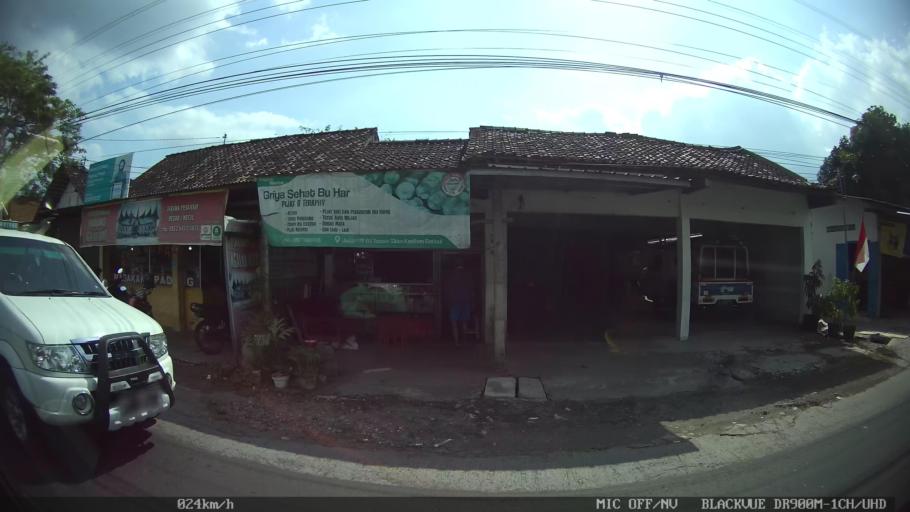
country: ID
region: Daerah Istimewa Yogyakarta
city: Kasihan
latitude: -7.8217
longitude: 110.3282
